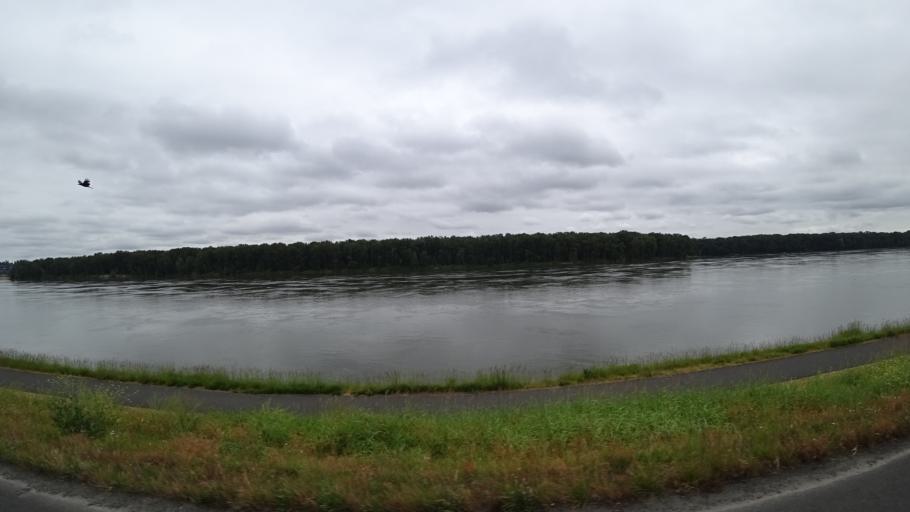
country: US
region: Washington
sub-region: Clark County
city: Orchards
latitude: 45.5852
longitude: -122.5669
